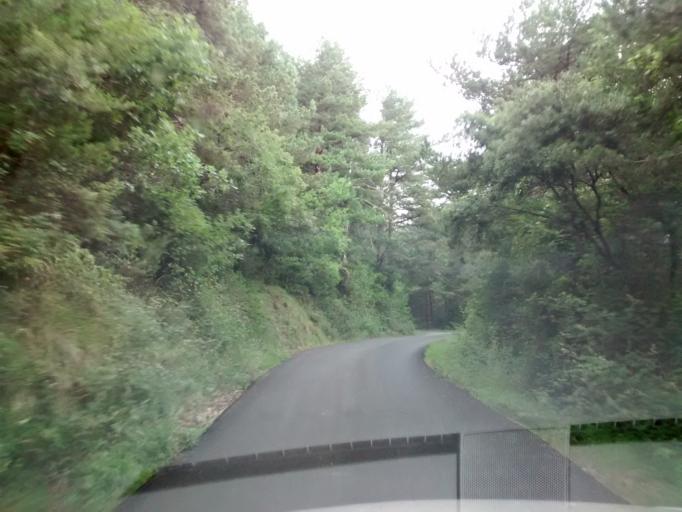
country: ES
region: Aragon
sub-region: Provincia de Huesca
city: Puertolas
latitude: 42.5614
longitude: 0.1405
